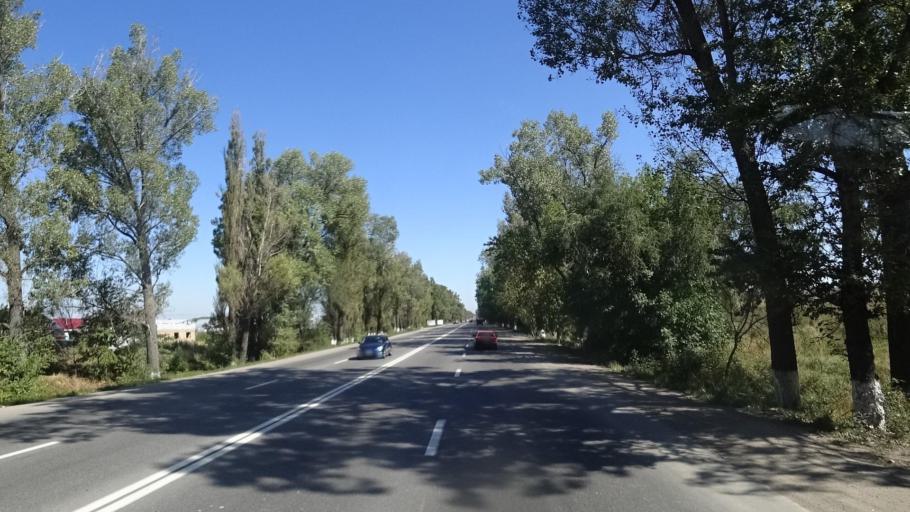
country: KZ
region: Almaty Oblysy
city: Energeticheskiy
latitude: 43.3603
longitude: 77.0774
